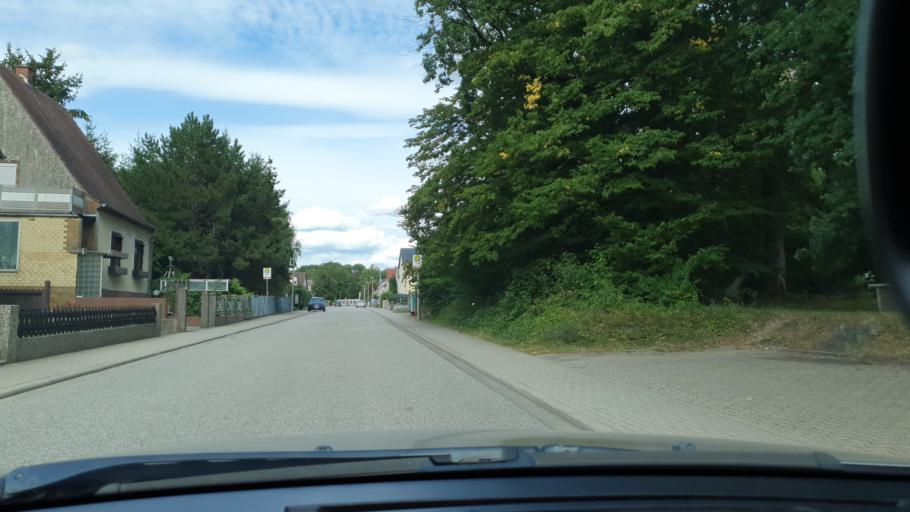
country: DE
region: Rheinland-Pfalz
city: Hoheischweiler
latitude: 49.2322
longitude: 7.5540
